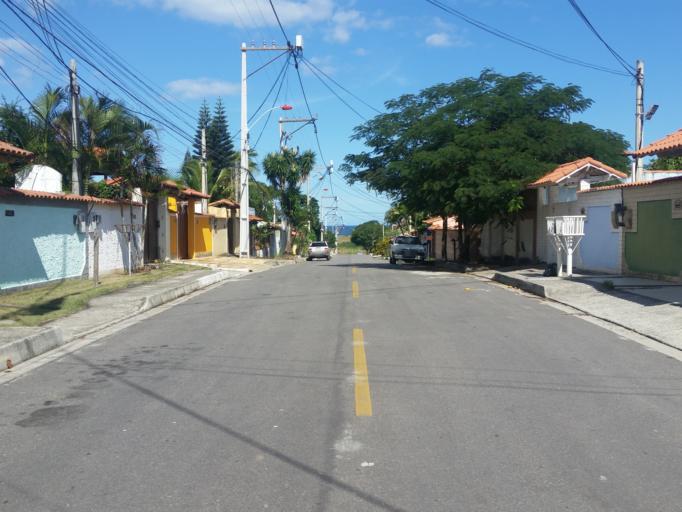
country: BR
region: Rio de Janeiro
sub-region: Marica
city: Marica
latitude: -22.9655
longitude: -42.9667
